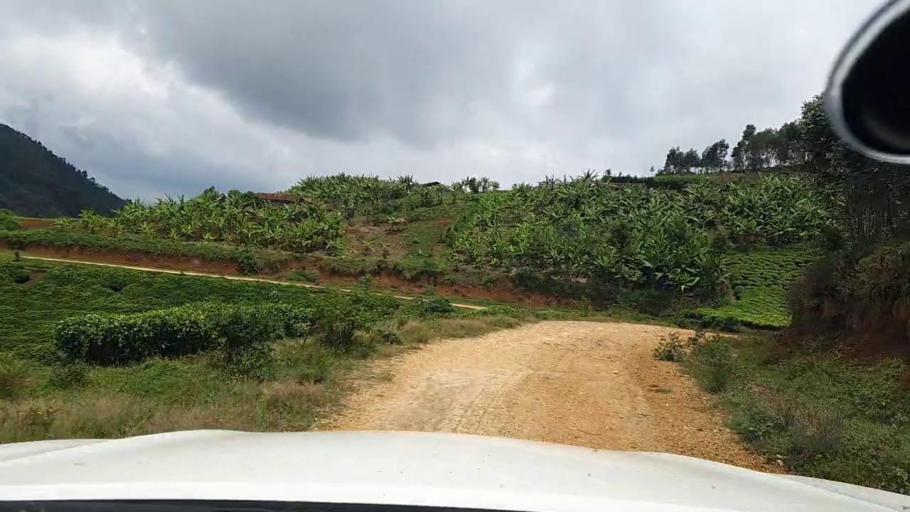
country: RW
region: Western Province
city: Kibuye
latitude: -2.1564
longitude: 29.4525
